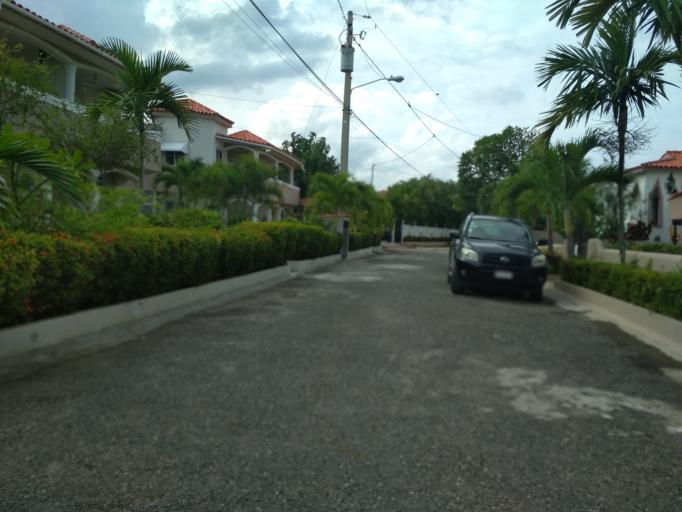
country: DO
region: Puerto Plata
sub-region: Puerto Plata
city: Puerto Plata
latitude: 19.8135
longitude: -70.7136
